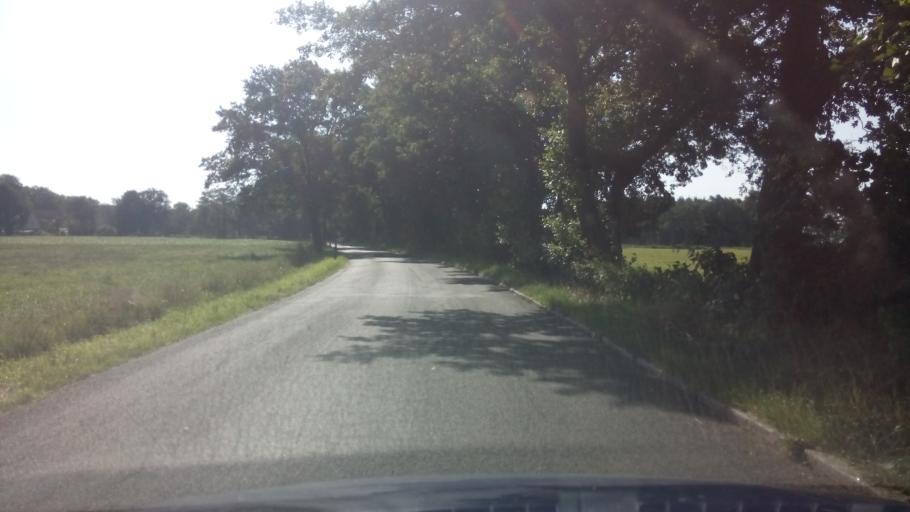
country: DE
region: Lower Saxony
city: Lilienthal
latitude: 53.1422
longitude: 8.9393
